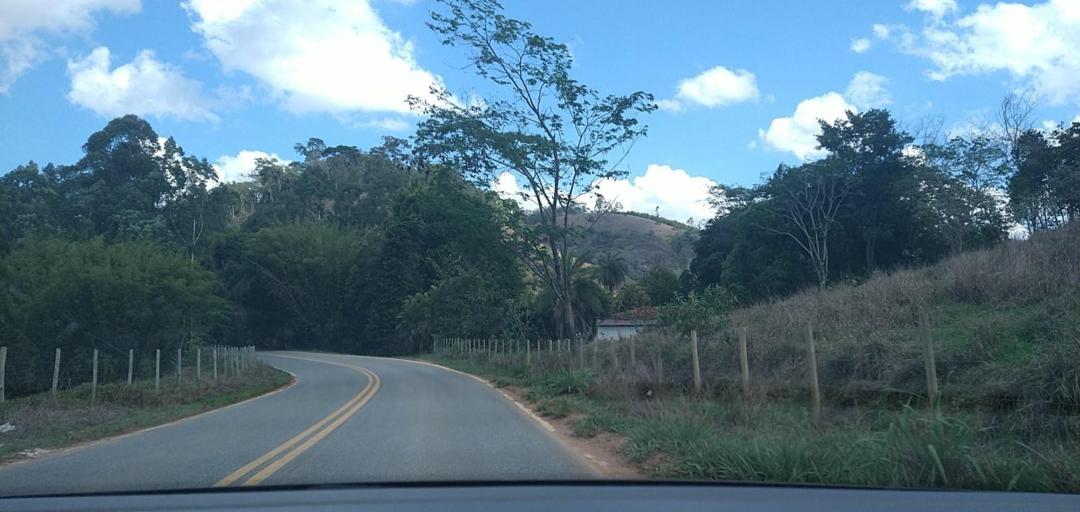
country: BR
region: Minas Gerais
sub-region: Rio Piracicaba
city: Rio Piracicaba
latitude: -20.0007
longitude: -43.1062
